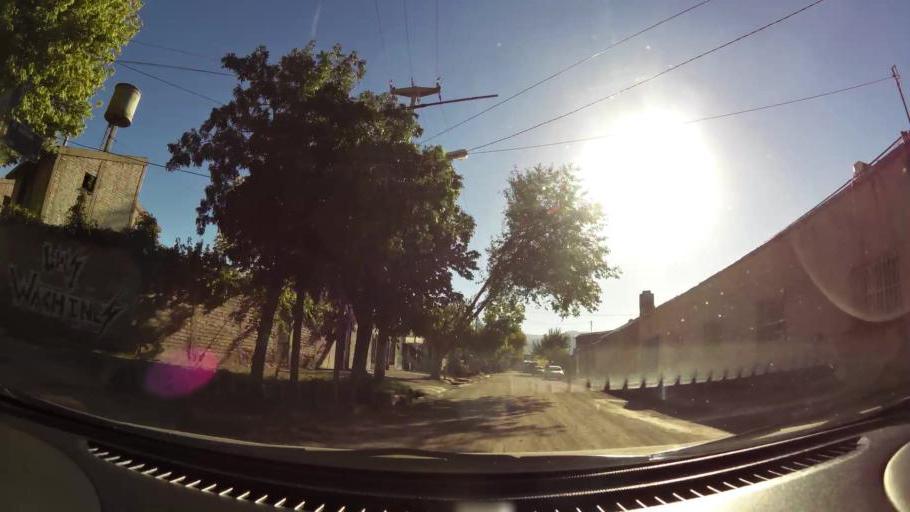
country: AR
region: Mendoza
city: Las Heras
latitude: -32.8492
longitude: -68.8274
